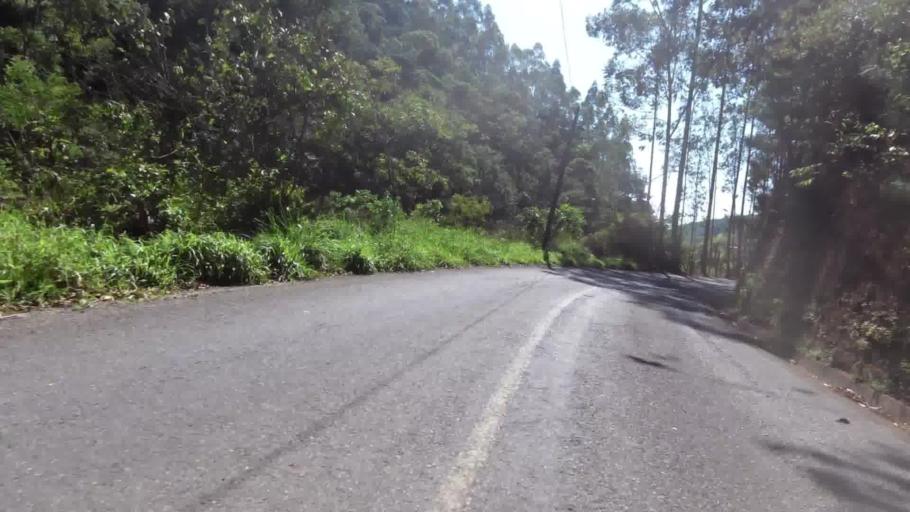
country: BR
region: Espirito Santo
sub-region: Marechal Floriano
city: Marechal Floriano
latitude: -20.4474
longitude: -40.8877
